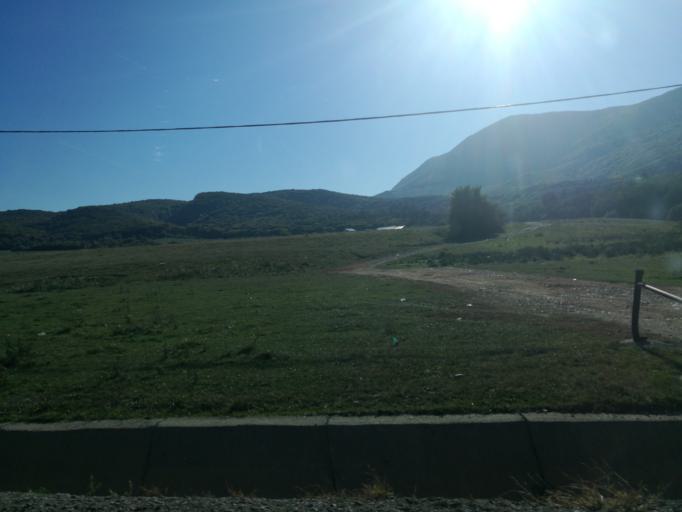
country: RO
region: Brasov
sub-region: Comuna Dumbravita
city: Dumbravita
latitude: 45.7335
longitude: 25.4400
